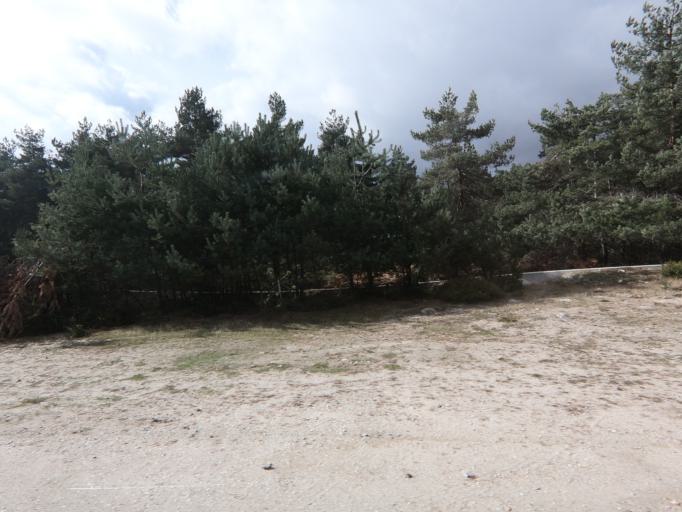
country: PT
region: Vila Real
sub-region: Vila Real
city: Vila Real
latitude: 41.3539
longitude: -7.7922
